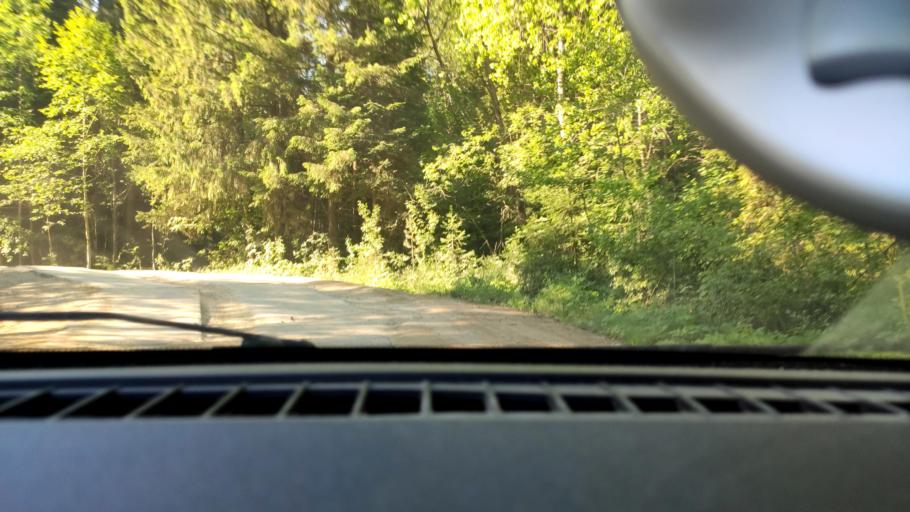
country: RU
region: Perm
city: Novyye Lyady
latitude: 58.1770
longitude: 56.5680
